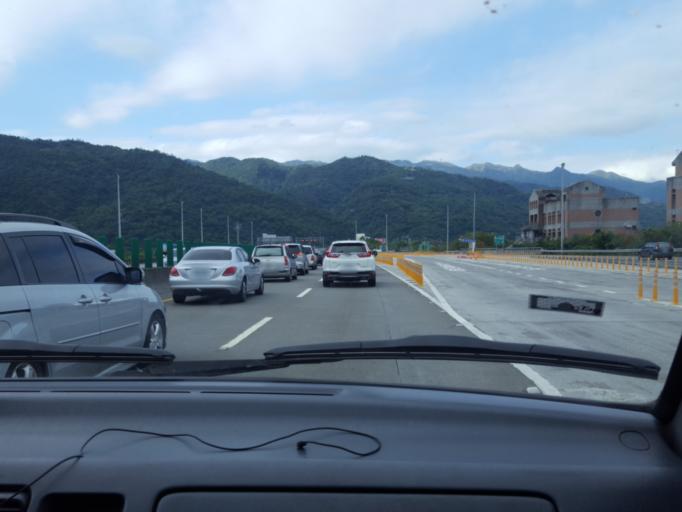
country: TW
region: Taiwan
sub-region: Yilan
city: Yilan
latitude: 24.8329
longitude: 121.7909
